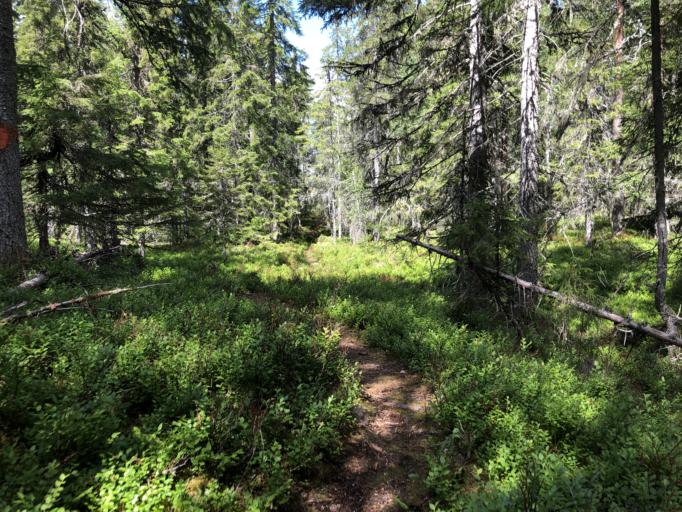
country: SE
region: Dalarna
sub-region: Vansbro Kommun
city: Jarna
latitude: 60.6681
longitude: 14.2709
